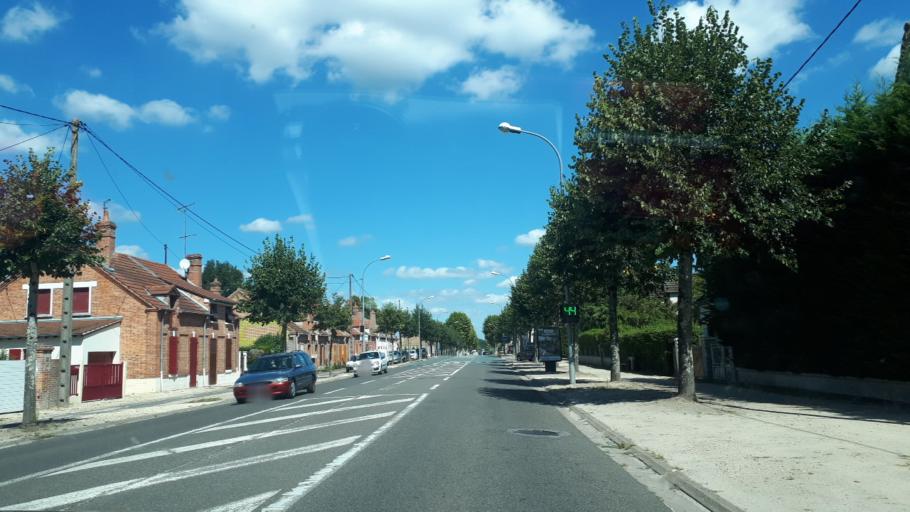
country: FR
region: Centre
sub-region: Departement du Loir-et-Cher
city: Lamotte-Beuvron
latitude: 47.5887
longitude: 2.0247
